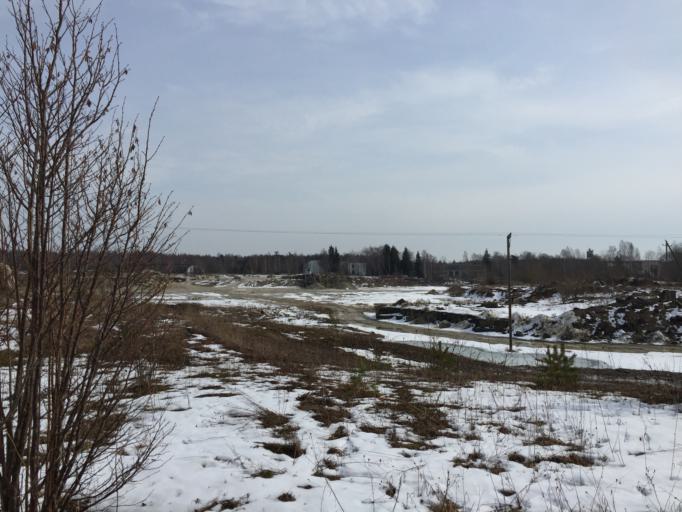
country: EE
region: Saare
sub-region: Kuressaare linn
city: Kuressaare
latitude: 58.3377
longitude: 22.4707
